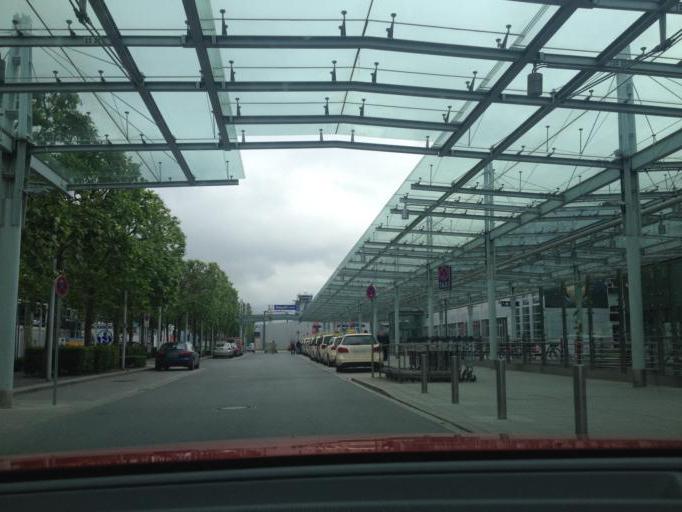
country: DE
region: Bavaria
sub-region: Regierungsbezirk Mittelfranken
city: Nuernberg
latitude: 49.4938
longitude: 11.0787
